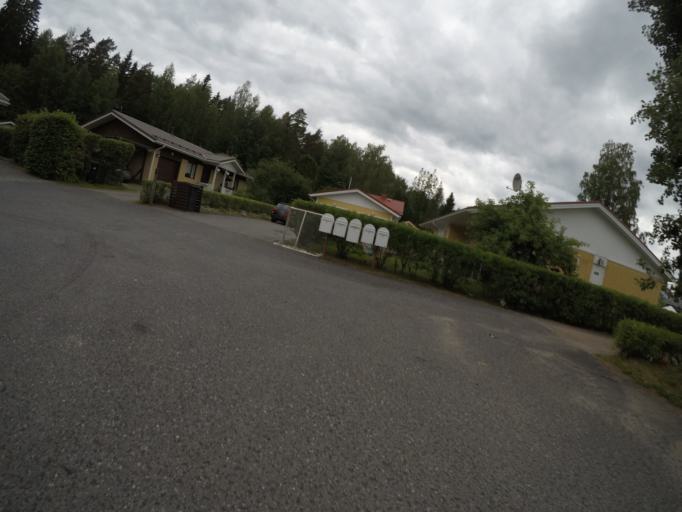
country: FI
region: Haeme
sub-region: Haemeenlinna
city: Haemeenlinna
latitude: 60.9762
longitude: 24.4666
